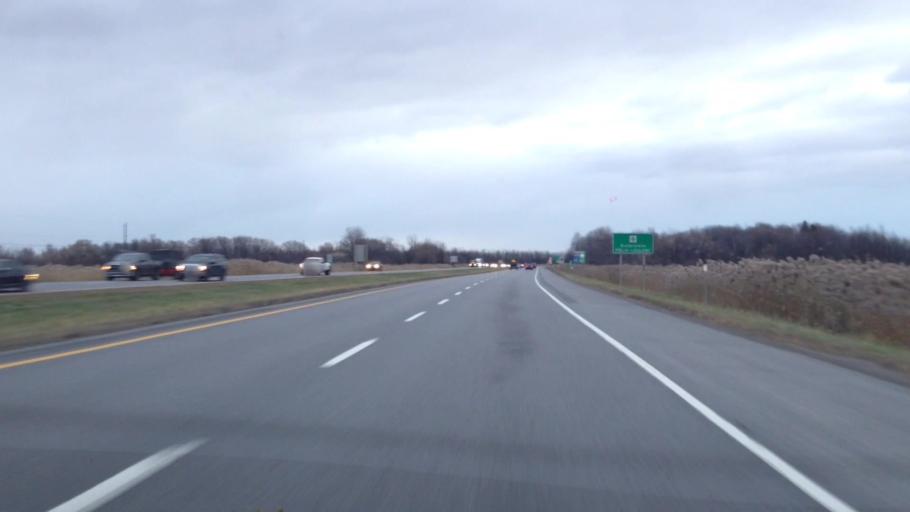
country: CA
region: Quebec
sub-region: Laurentides
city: Oka
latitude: 45.4248
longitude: -74.0979
